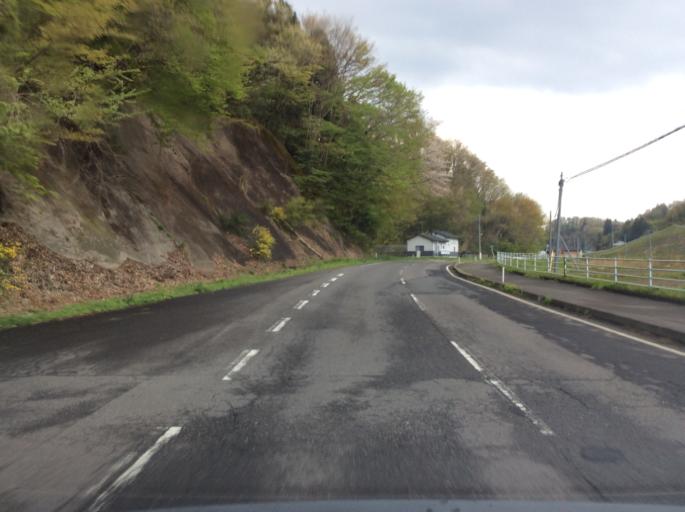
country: JP
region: Fukushima
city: Funehikimachi-funehiki
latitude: 37.4095
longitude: 140.5415
